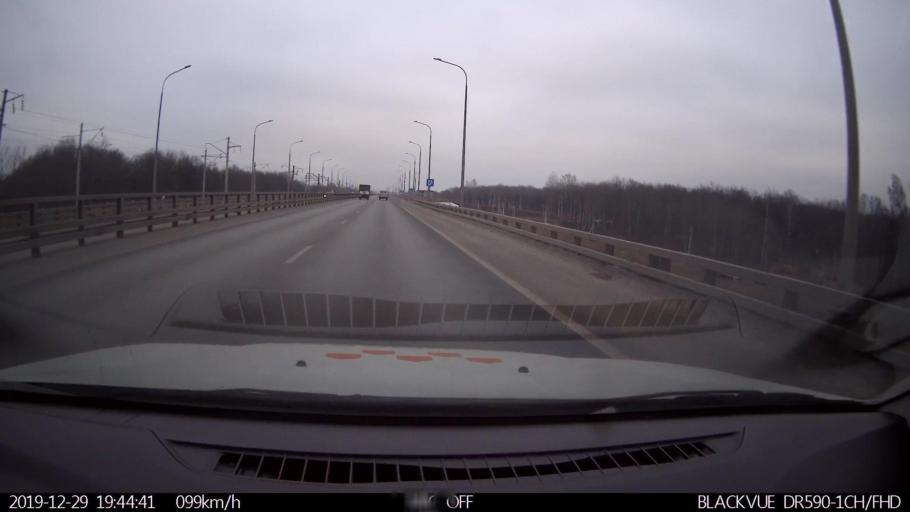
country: RU
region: Nizjnij Novgorod
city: Neklyudovo
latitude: 56.3778
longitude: 43.9542
